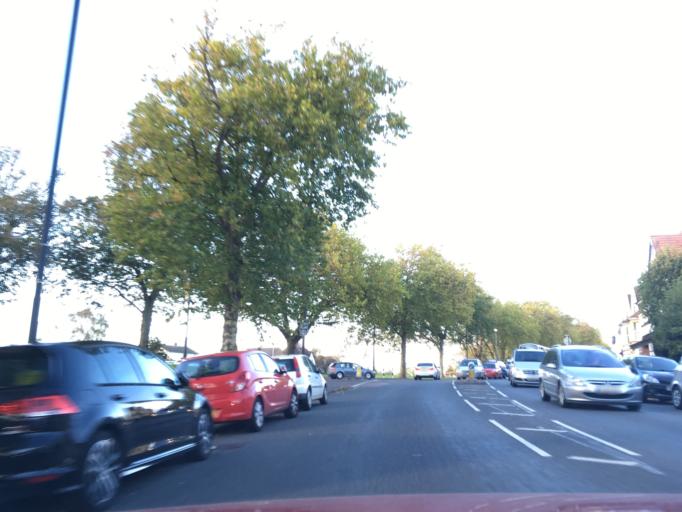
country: GB
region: England
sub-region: Bristol
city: Bristol
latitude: 51.4903
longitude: -2.5852
